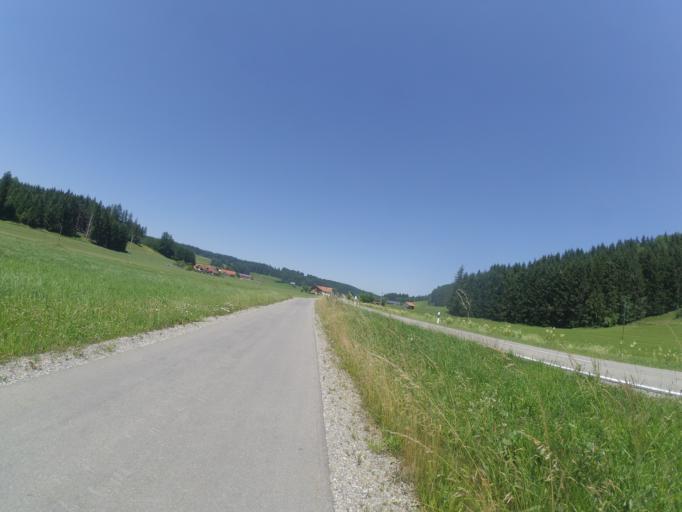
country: DE
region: Bavaria
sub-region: Swabia
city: Untrasried
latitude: 47.8386
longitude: 10.3564
